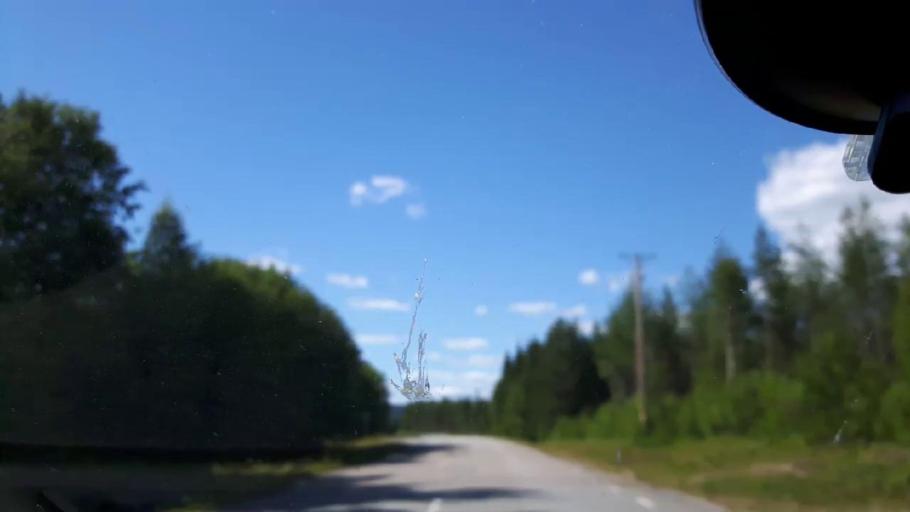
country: SE
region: Vaesternorrland
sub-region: Ange Kommun
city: Fransta
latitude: 62.7066
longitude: 16.3584
